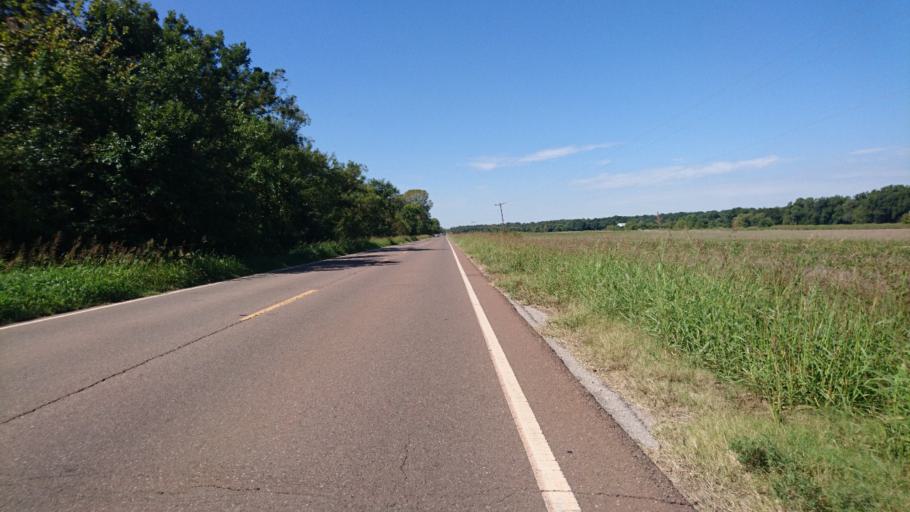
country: US
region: Oklahoma
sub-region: Oklahoma County
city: Luther
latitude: 35.6621
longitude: -97.2562
